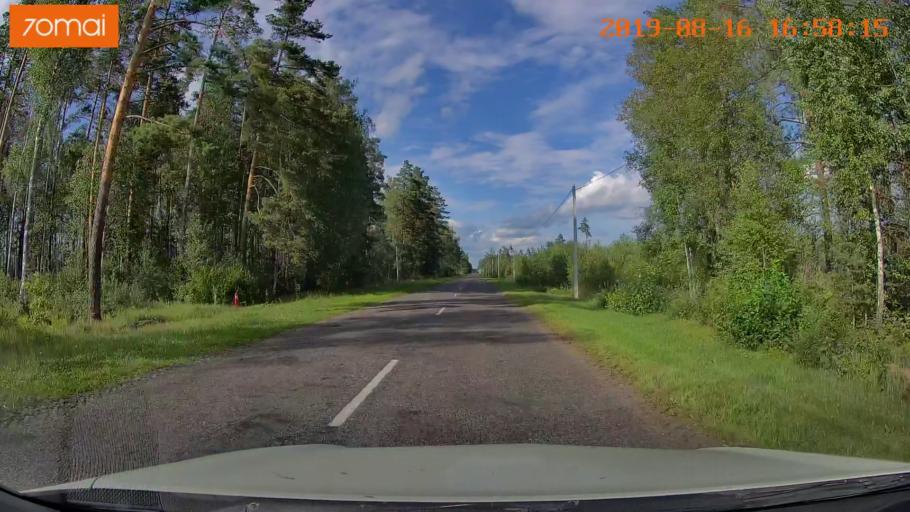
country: BY
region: Mogilev
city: Hlusha
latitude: 53.2667
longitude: 28.8316
